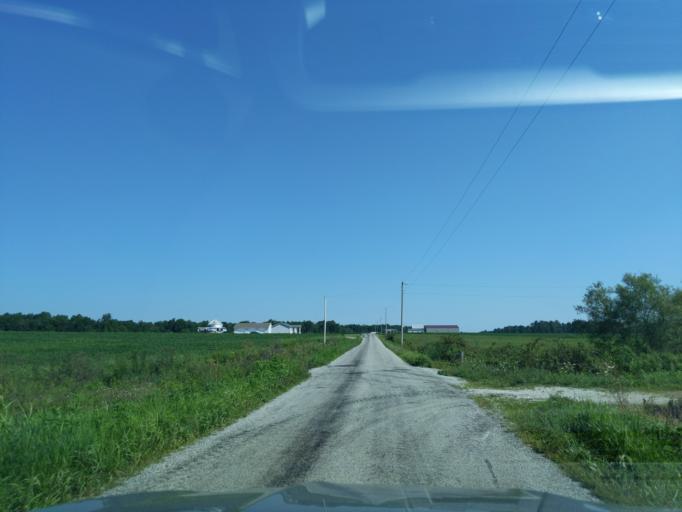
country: US
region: Indiana
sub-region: Ripley County
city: Osgood
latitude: 39.0830
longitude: -85.4332
